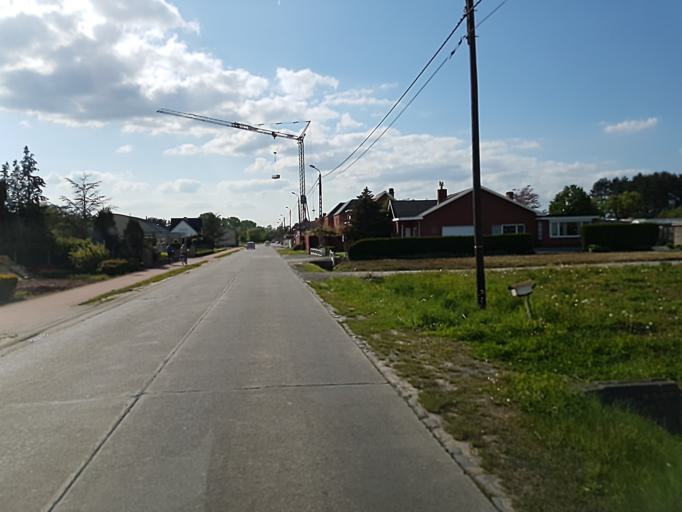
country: BE
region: Flanders
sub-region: Provincie Vlaams-Brabant
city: Begijnendijk
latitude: 51.0247
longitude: 4.7500
